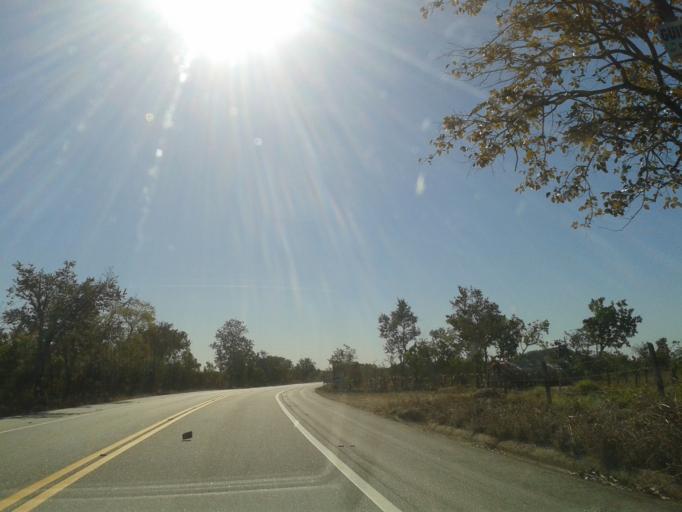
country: BR
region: Goias
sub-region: Itapuranga
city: Itapuranga
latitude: -15.4929
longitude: -50.3198
